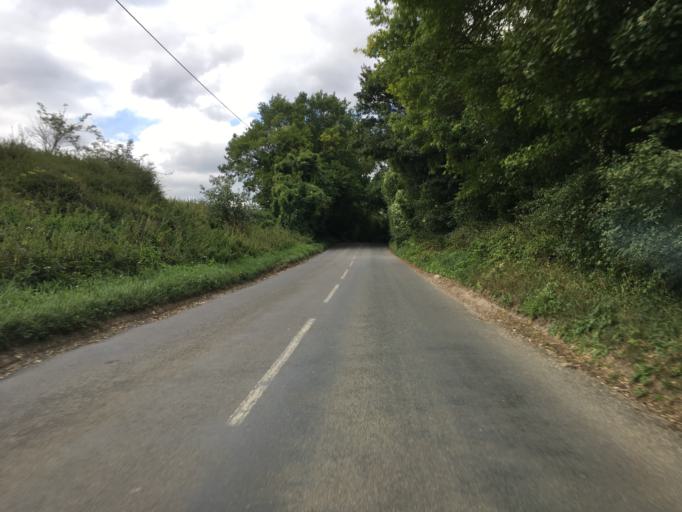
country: GB
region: England
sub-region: Hampshire
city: Overton
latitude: 51.2261
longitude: -1.2617
